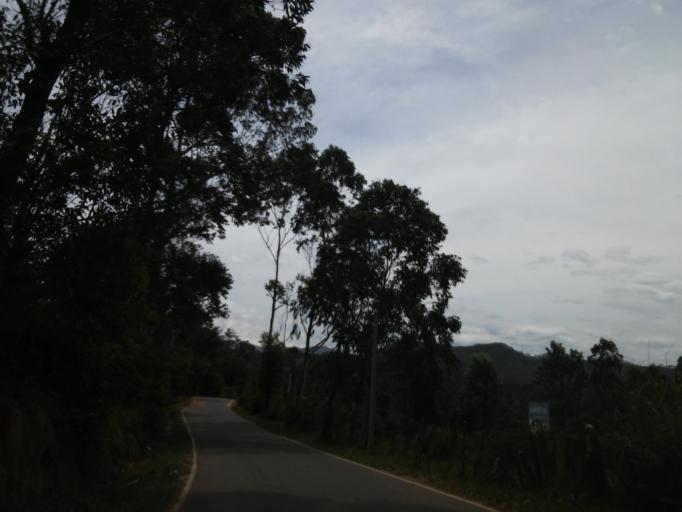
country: LK
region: Uva
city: Haputale
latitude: 6.8469
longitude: 81.0203
